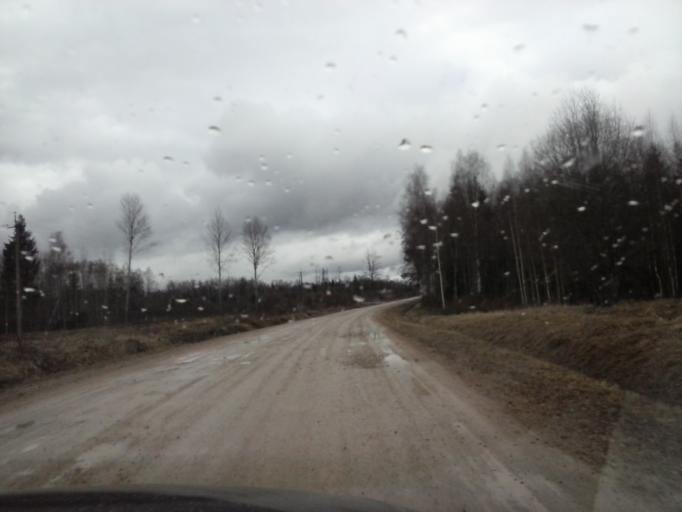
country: EE
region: Ida-Virumaa
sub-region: Kivioli linn
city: Kivioli
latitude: 59.1057
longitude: 26.9164
